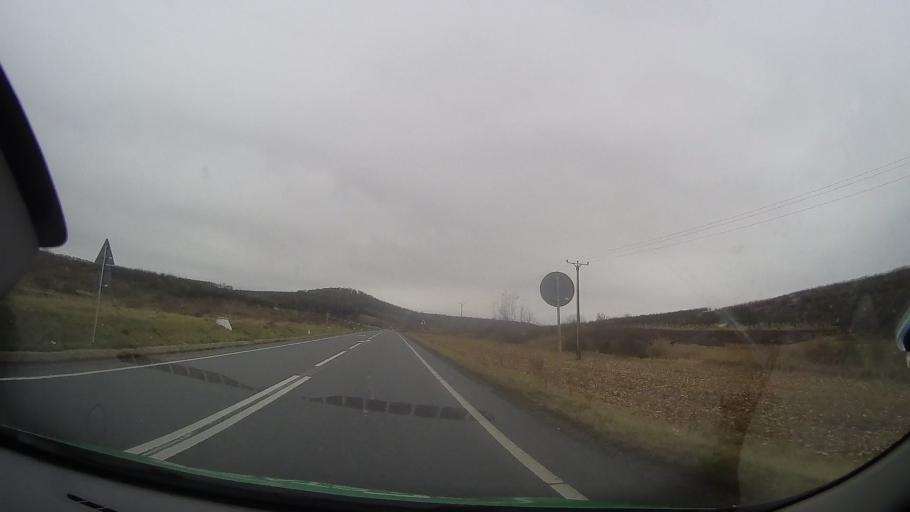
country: RO
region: Mures
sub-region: Comuna Breaza
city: Breaza
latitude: 46.7837
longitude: 24.6515
